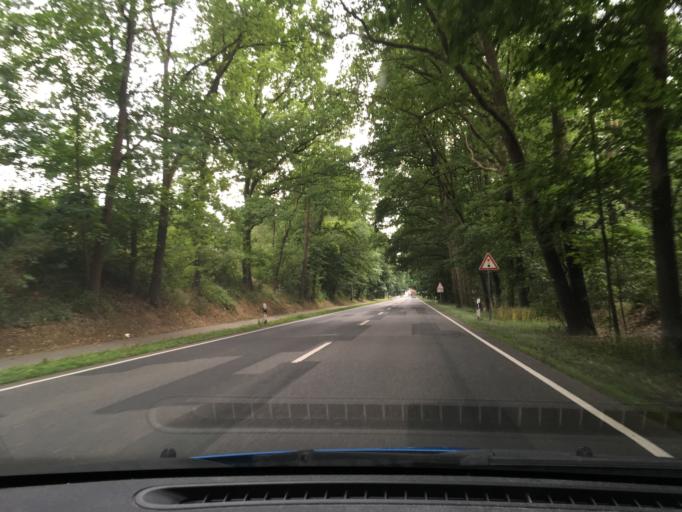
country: DE
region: Lower Saxony
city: Kakenstorf
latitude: 53.3073
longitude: 9.7578
